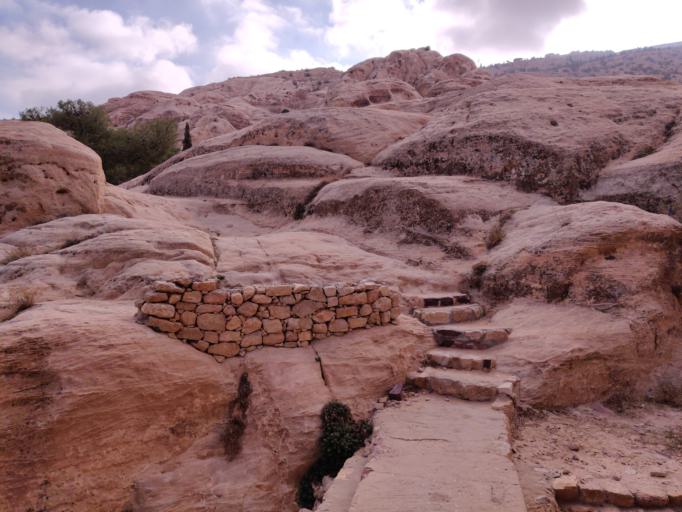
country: JO
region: Ma'an
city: Petra
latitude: 30.3197
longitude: 35.4608
